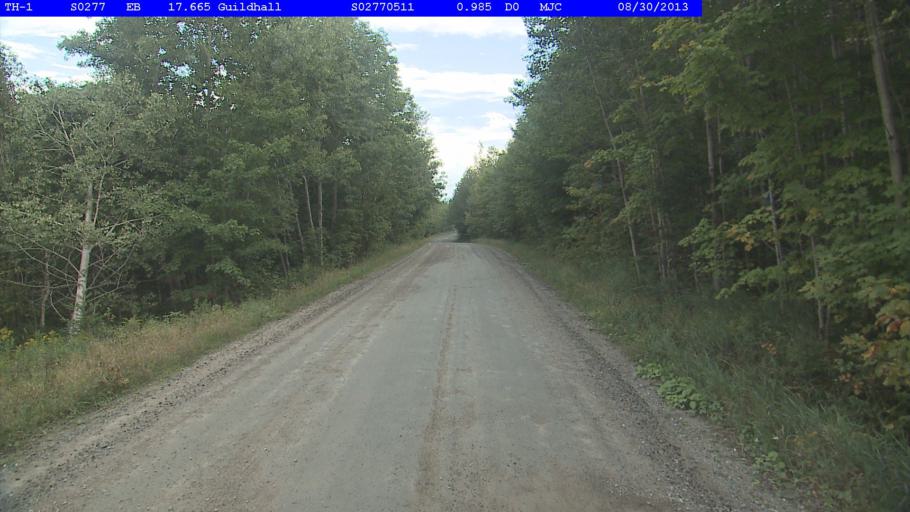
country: US
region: Vermont
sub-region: Essex County
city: Guildhall
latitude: 44.5704
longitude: -71.6508
